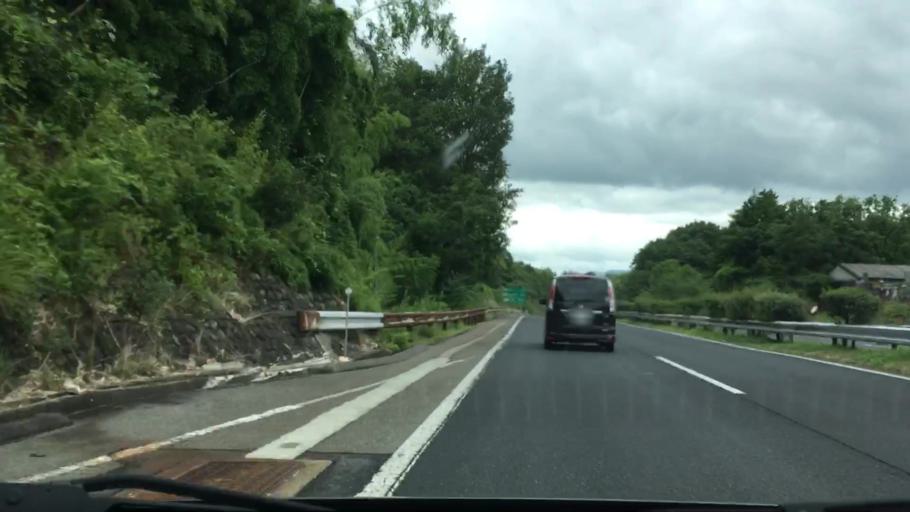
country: JP
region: Okayama
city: Tsuyama
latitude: 35.0701
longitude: 134.0343
